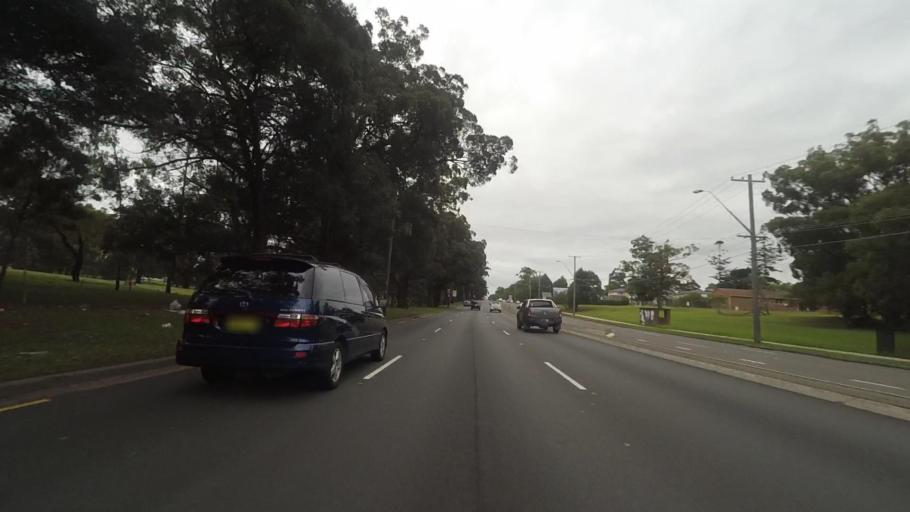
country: AU
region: New South Wales
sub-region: Auburn
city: Berala
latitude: -33.8833
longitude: 151.0402
